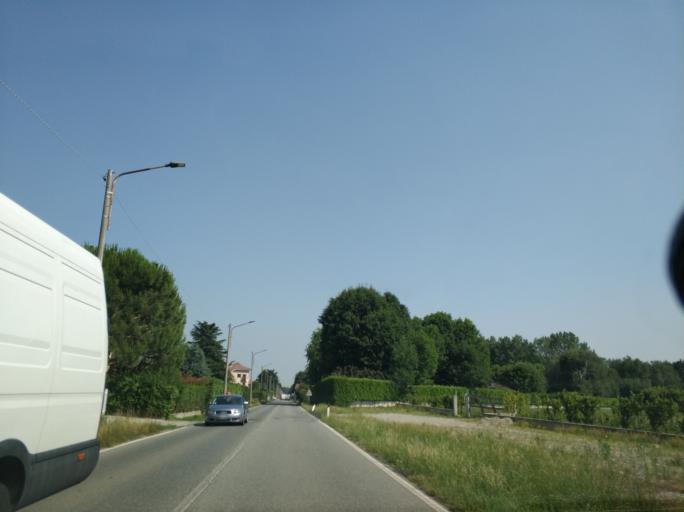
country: IT
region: Piedmont
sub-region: Provincia di Torino
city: Oglianico
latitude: 45.3453
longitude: 7.7077
